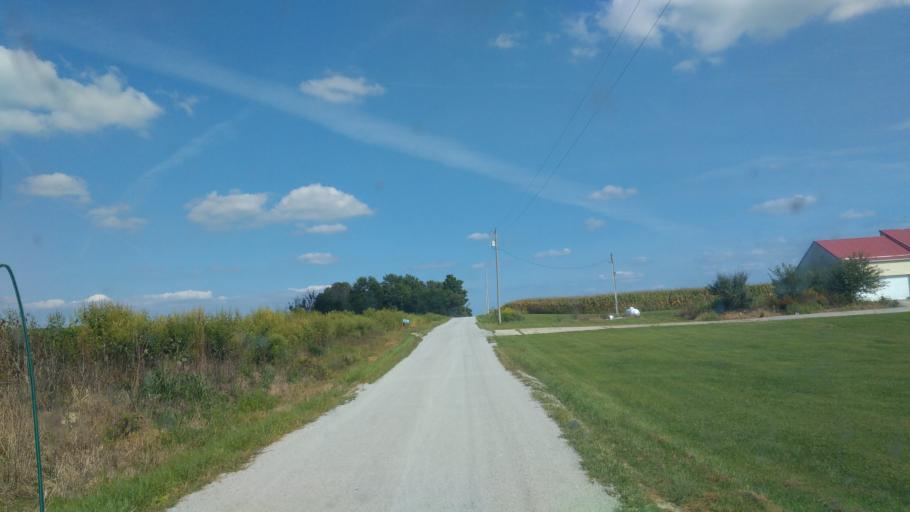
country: US
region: Ohio
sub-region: Hardin County
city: Kenton
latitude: 40.6291
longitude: -83.4572
